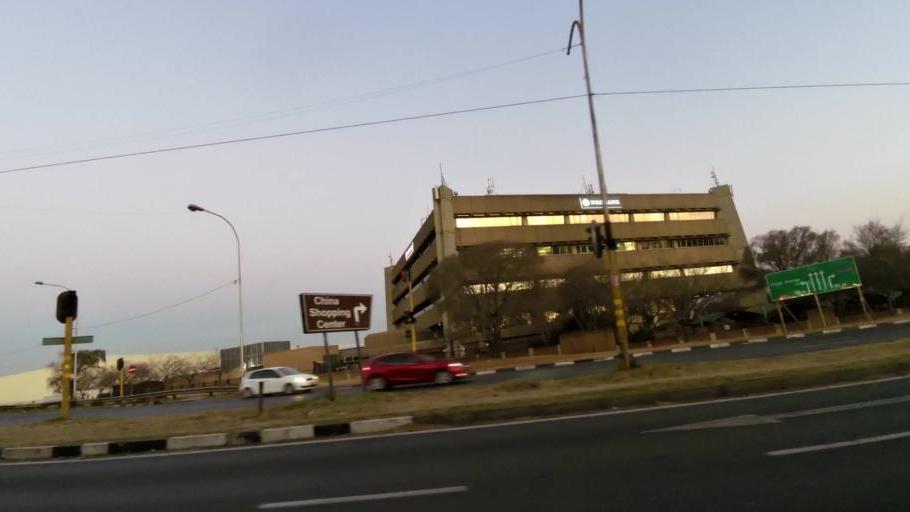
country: ZA
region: Gauteng
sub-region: City of Johannesburg Metropolitan Municipality
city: Johannesburg
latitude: -26.2143
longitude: 28.0147
